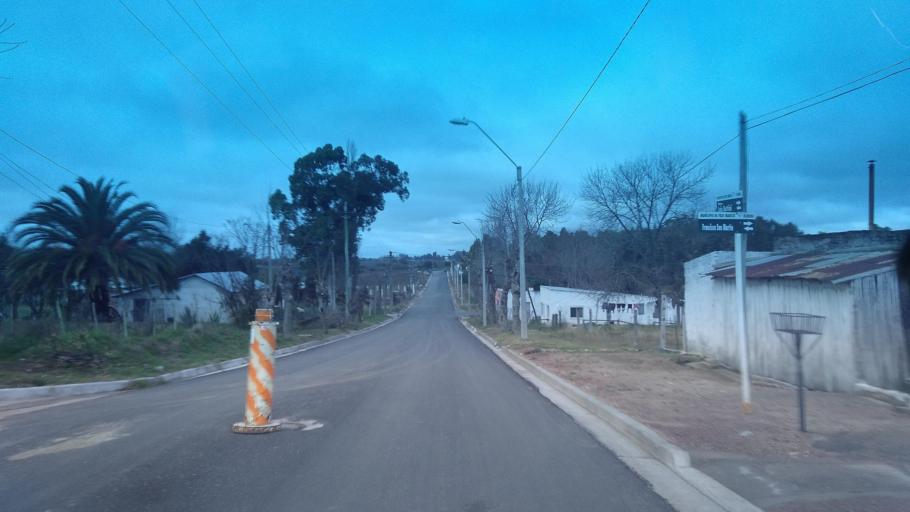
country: UY
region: Canelones
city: Tala
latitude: -34.2016
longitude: -55.7403
